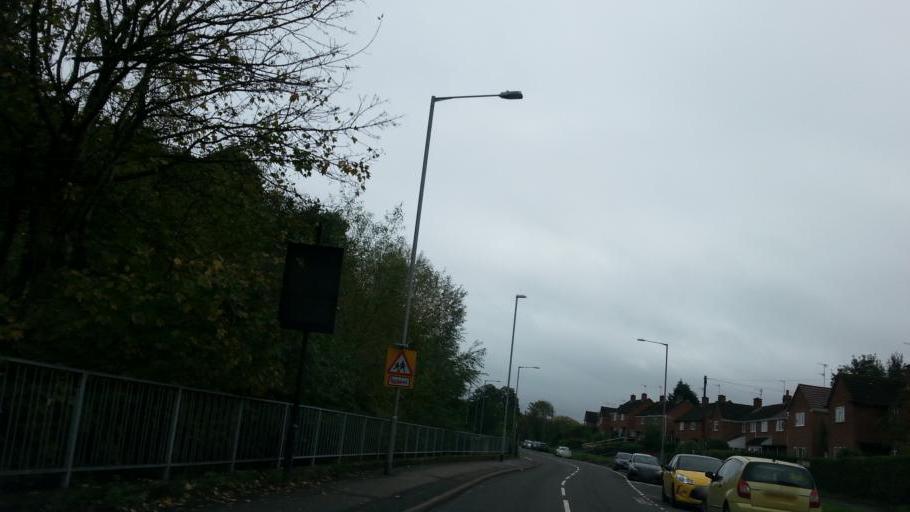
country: GB
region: England
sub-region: Worcestershire
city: Bromsgrove
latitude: 52.3254
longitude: -2.0661
